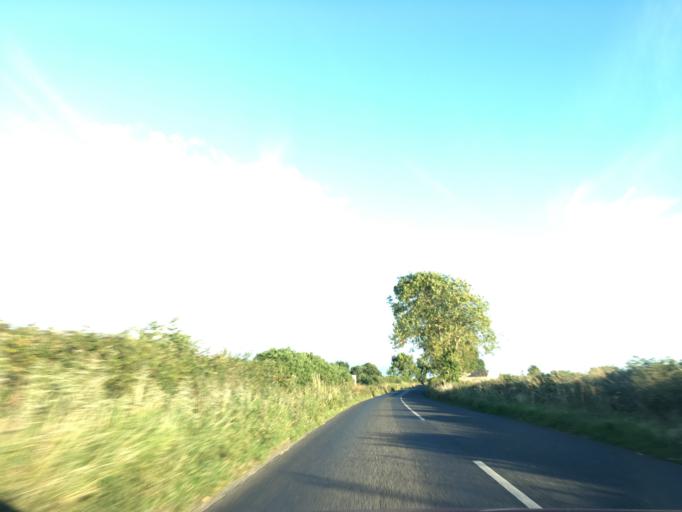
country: IE
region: Munster
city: Cashel
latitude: 52.4770
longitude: -7.9271
